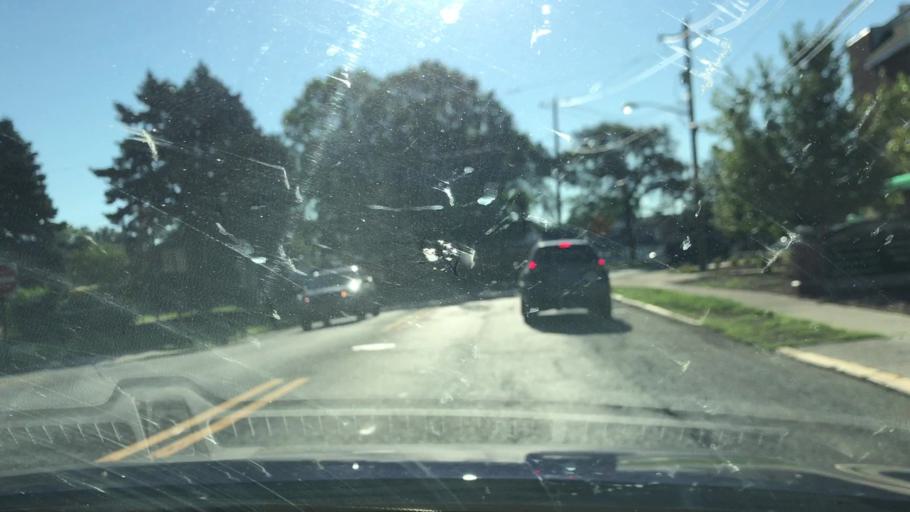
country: US
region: New Jersey
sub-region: Bergen County
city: Cresskill
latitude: 40.9418
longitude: -73.9636
